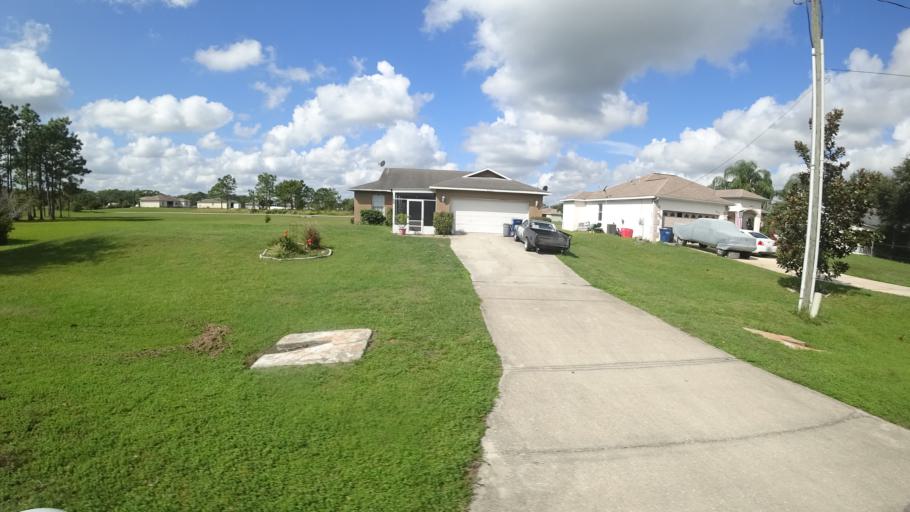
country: US
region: Florida
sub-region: Sarasota County
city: Lake Sarasota
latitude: 27.3896
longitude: -82.2712
